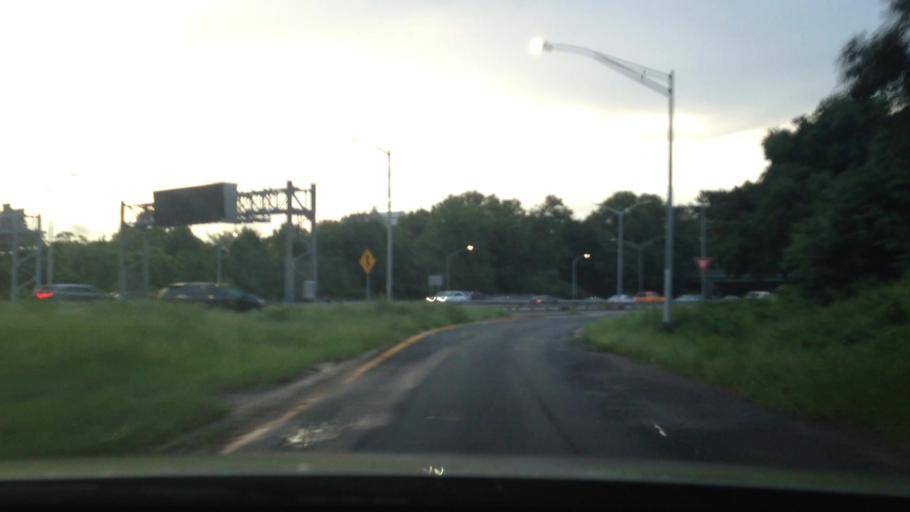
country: US
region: New York
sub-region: Queens County
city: Borough of Queens
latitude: 40.7422
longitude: -73.8454
